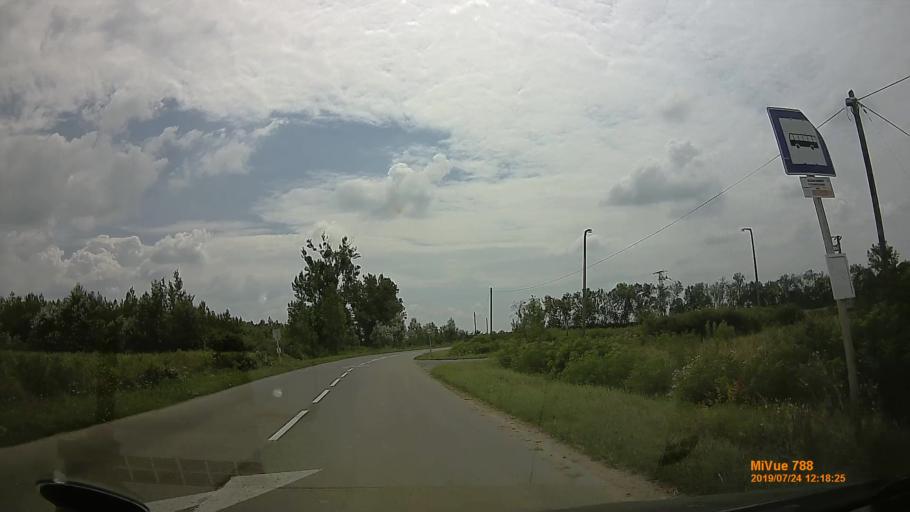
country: HU
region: Szabolcs-Szatmar-Bereg
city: Vasarosnameny
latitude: 48.1511
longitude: 22.3477
